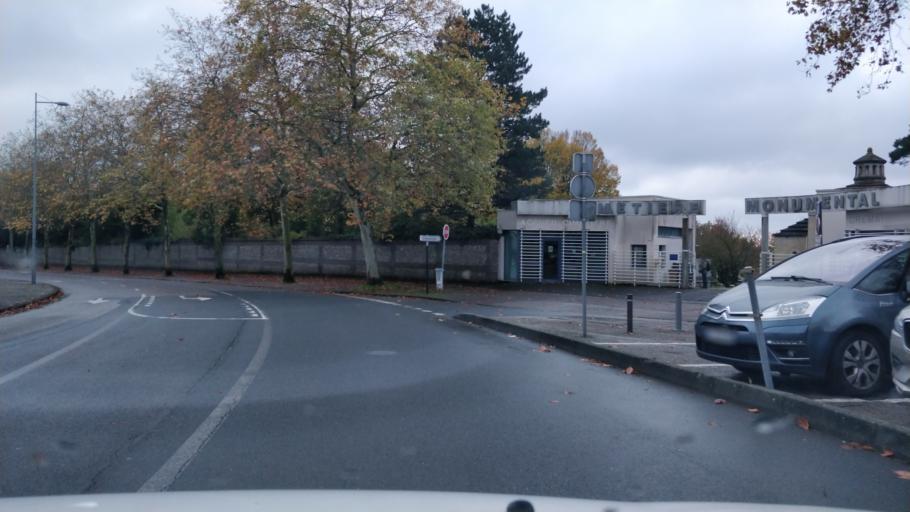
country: FR
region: Haute-Normandie
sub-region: Departement de la Seine-Maritime
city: Bihorel
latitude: 49.4519
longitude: 1.1196
